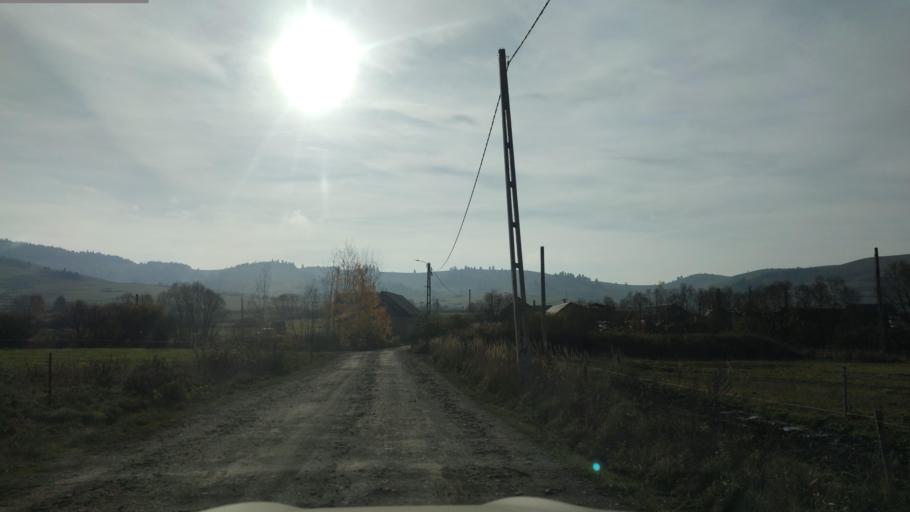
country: RO
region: Harghita
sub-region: Comuna Ditrau
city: Ditrau
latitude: 46.8224
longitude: 25.5362
